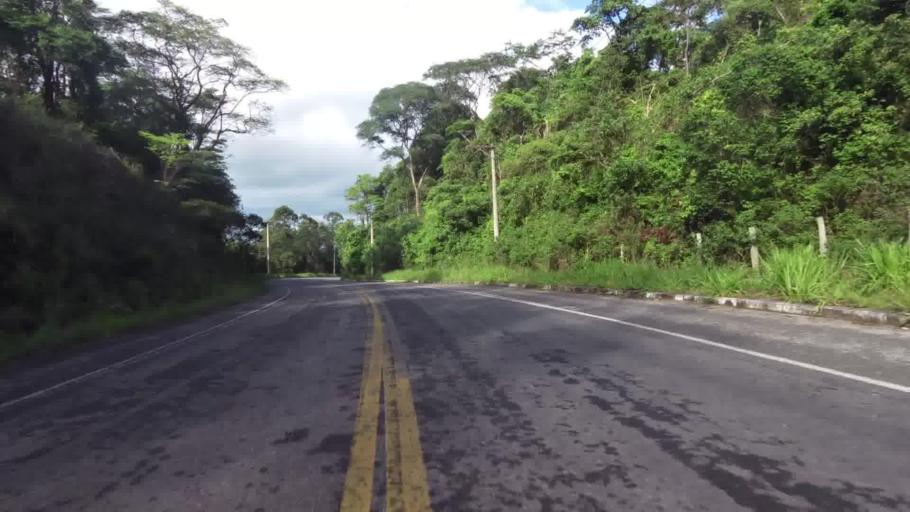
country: BR
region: Espirito Santo
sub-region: Piuma
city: Piuma
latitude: -20.7984
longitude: -40.6257
